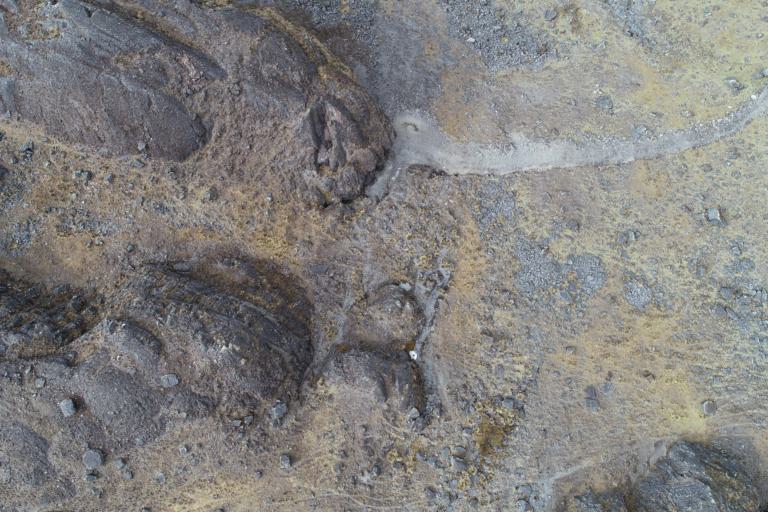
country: BO
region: La Paz
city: Sorata
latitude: -15.6687
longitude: -68.5526
